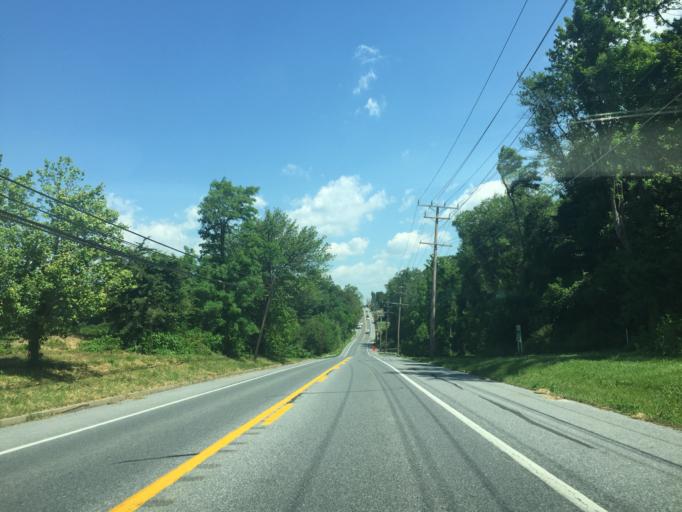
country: US
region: Maryland
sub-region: Baltimore County
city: Reisterstown
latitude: 39.5094
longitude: -76.8346
